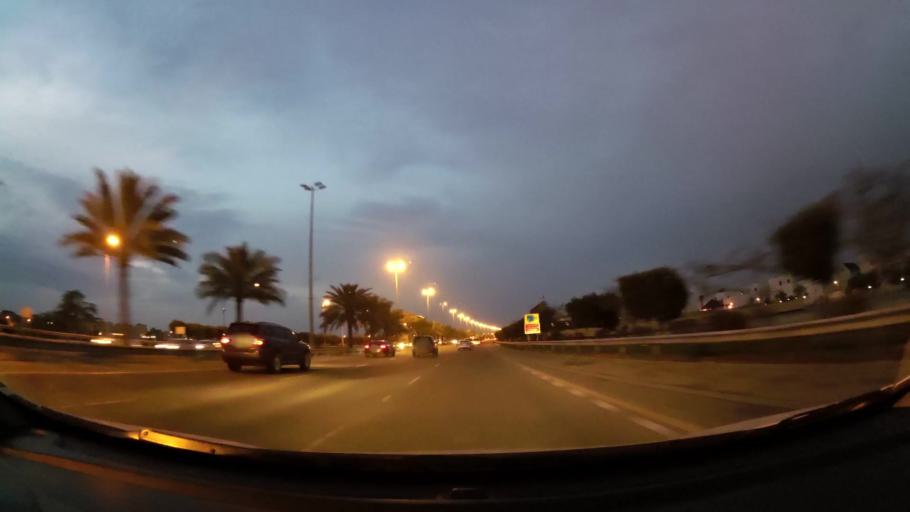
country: BH
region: Northern
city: Madinat `Isa
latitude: 26.1941
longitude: 50.5067
